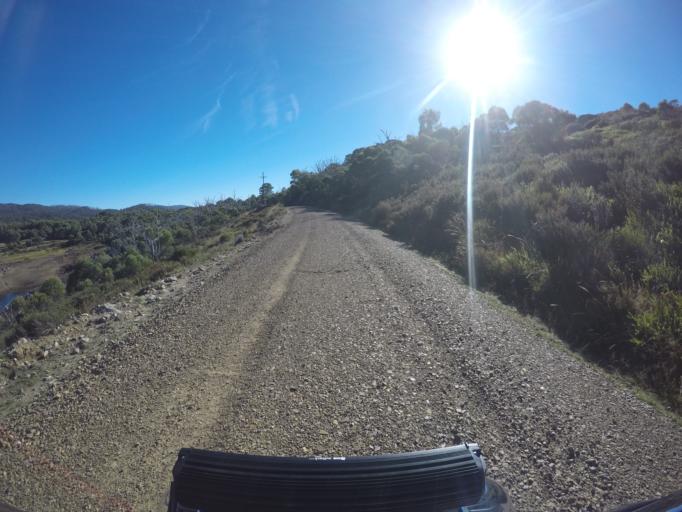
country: AU
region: New South Wales
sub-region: Snowy River
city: Jindabyne
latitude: -36.0538
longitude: 148.2794
